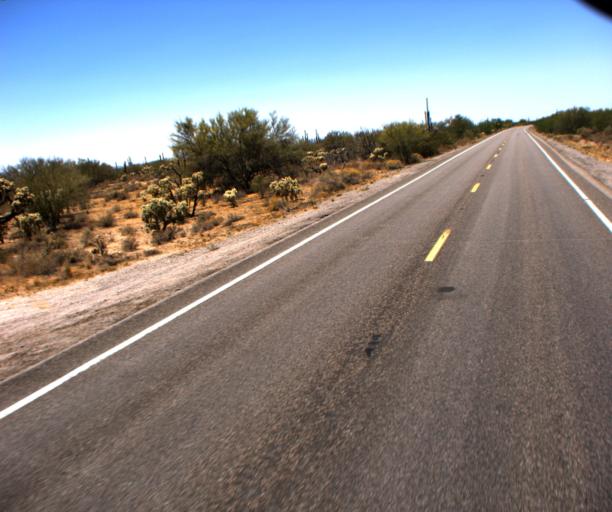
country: US
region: Arizona
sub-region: Pima County
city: Marana
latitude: 32.7661
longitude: -111.1533
